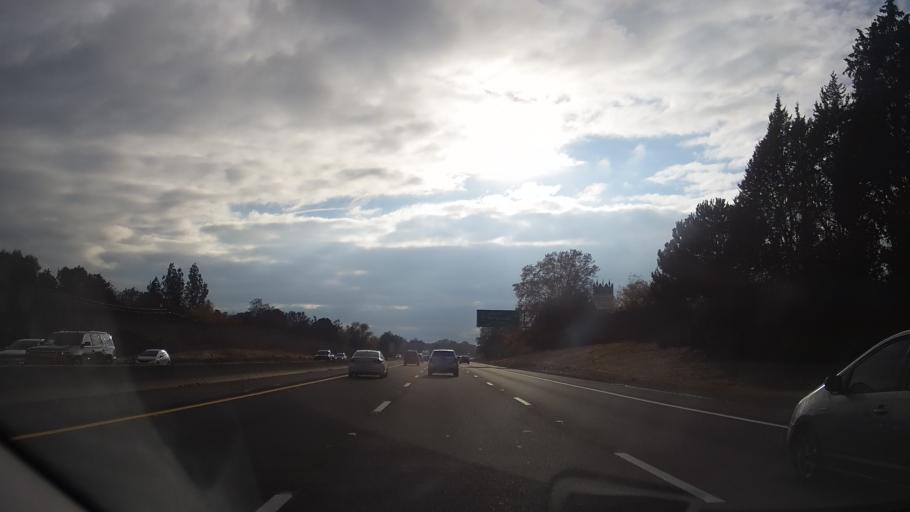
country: US
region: California
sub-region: Placer County
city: Rocklin
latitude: 38.7820
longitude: -121.2306
